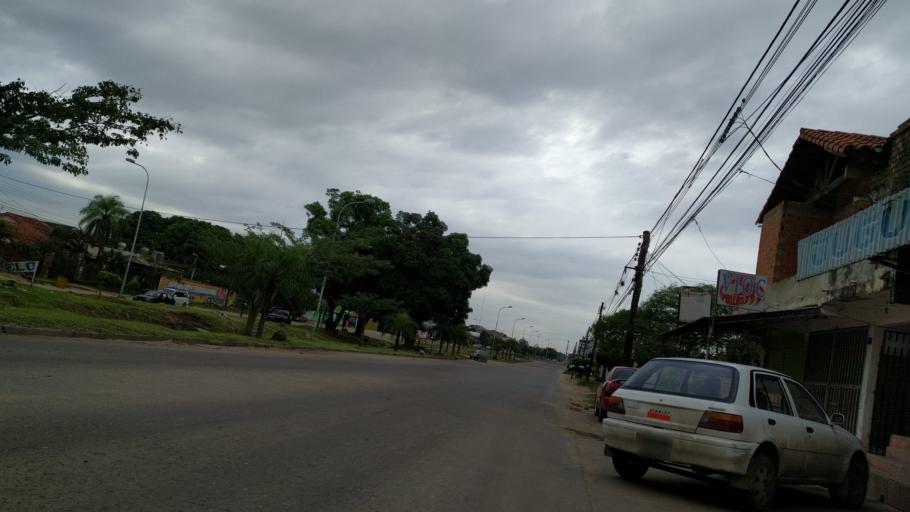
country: BO
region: Santa Cruz
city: Santa Cruz de la Sierra
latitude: -17.8138
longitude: -63.2215
